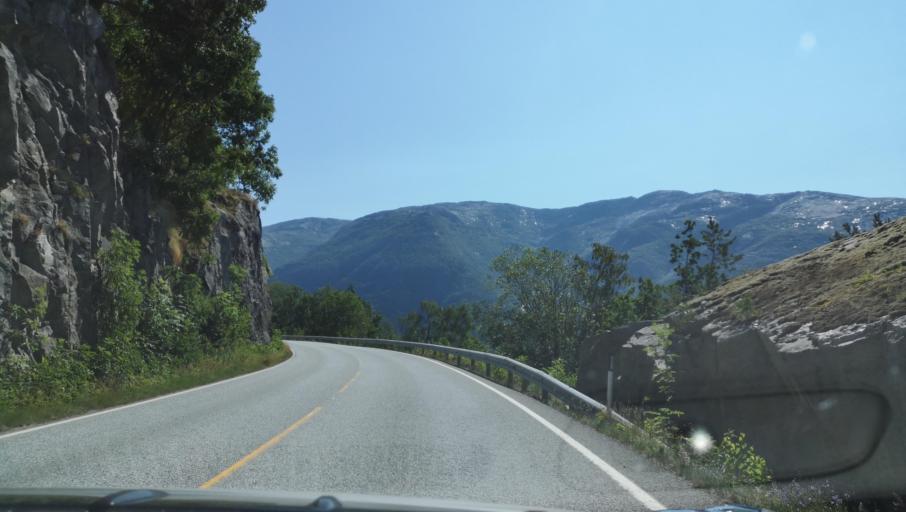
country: NO
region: Hordaland
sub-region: Ulvik
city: Ulvik
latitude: 60.4866
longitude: 6.8732
